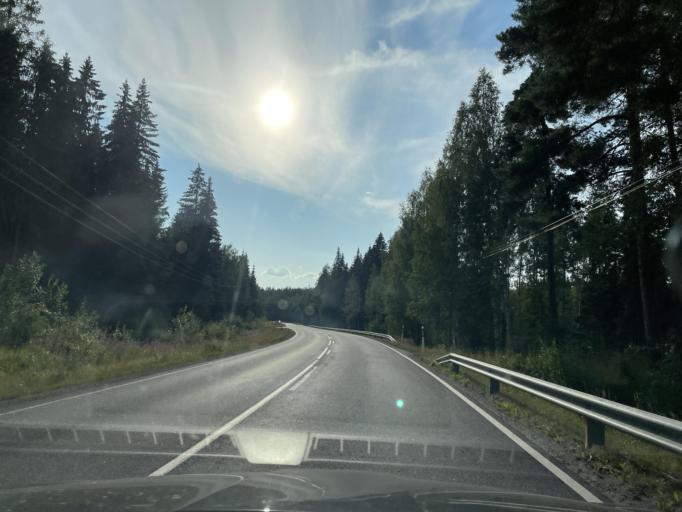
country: FI
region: Paijanne Tavastia
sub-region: Lahti
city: Padasjoki
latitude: 61.3274
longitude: 25.1883
